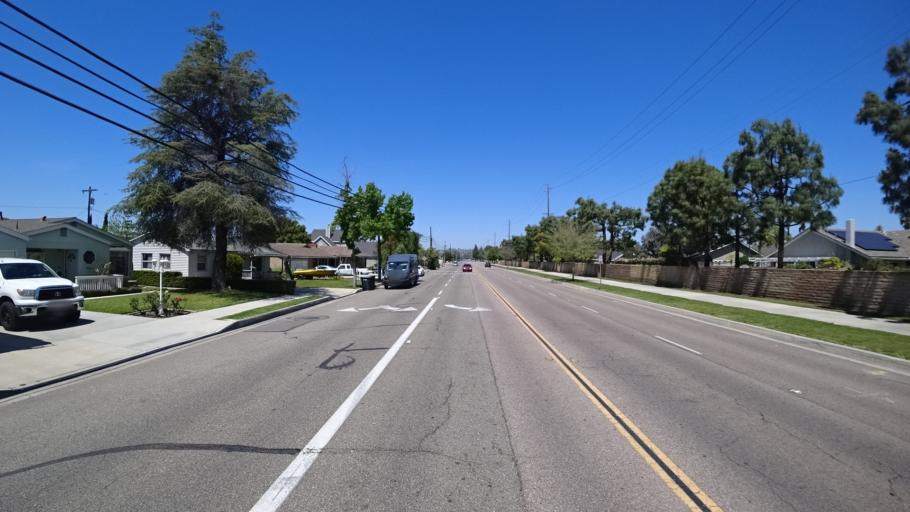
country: US
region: California
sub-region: Orange County
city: Villa Park
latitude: 33.8031
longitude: -117.8220
